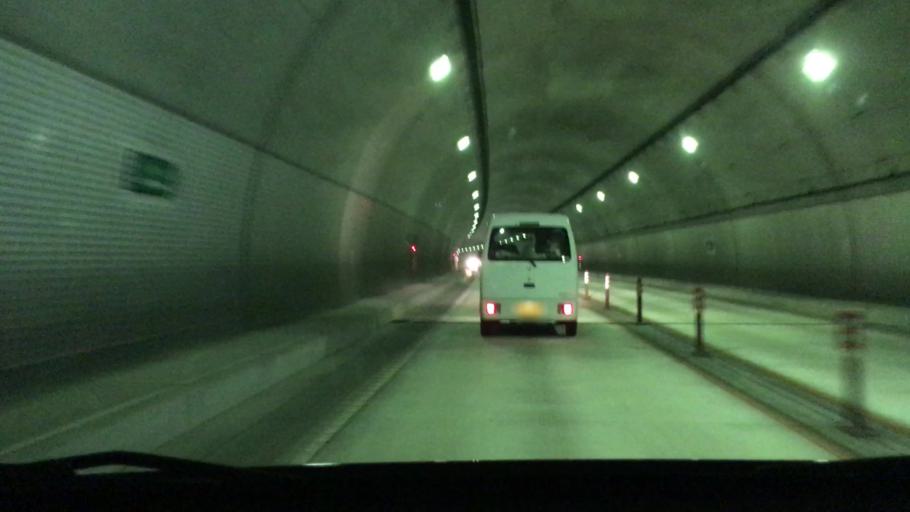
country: JP
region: Nagasaki
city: Sasebo
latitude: 33.0925
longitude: 129.7787
